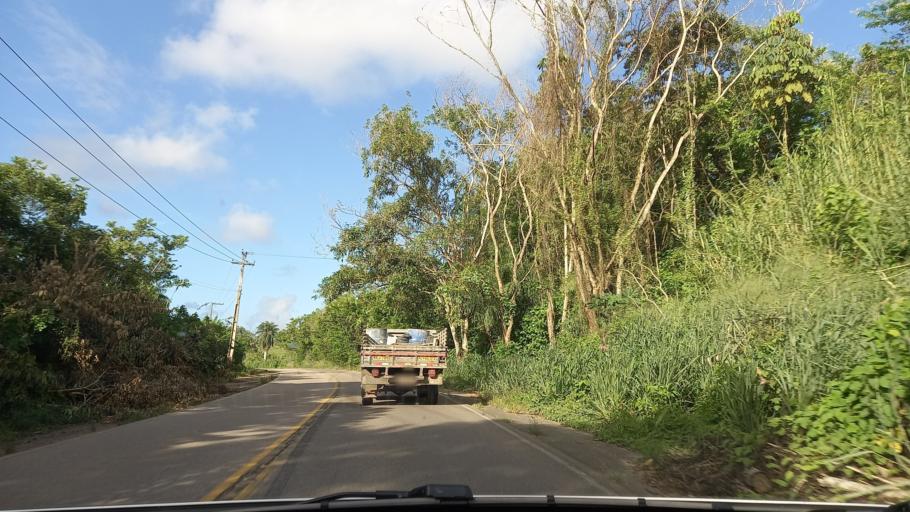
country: BR
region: Pernambuco
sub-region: Rio Formoso
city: Rio Formoso
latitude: -8.6562
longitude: -35.1384
